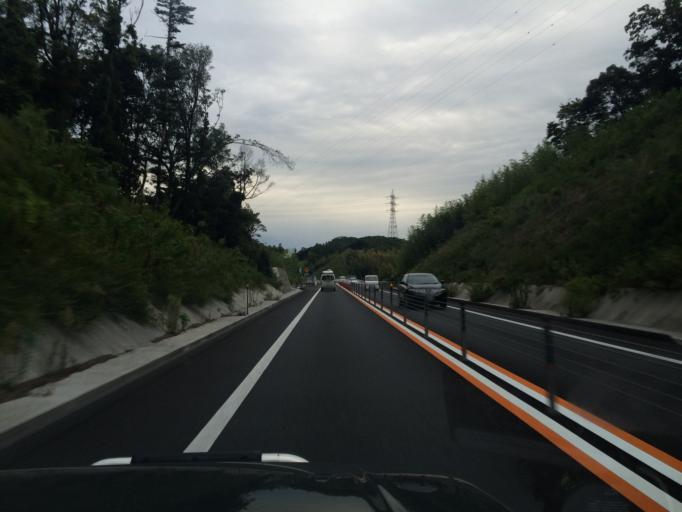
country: JP
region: Tottori
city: Tottori
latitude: 35.4956
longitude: 134.1759
